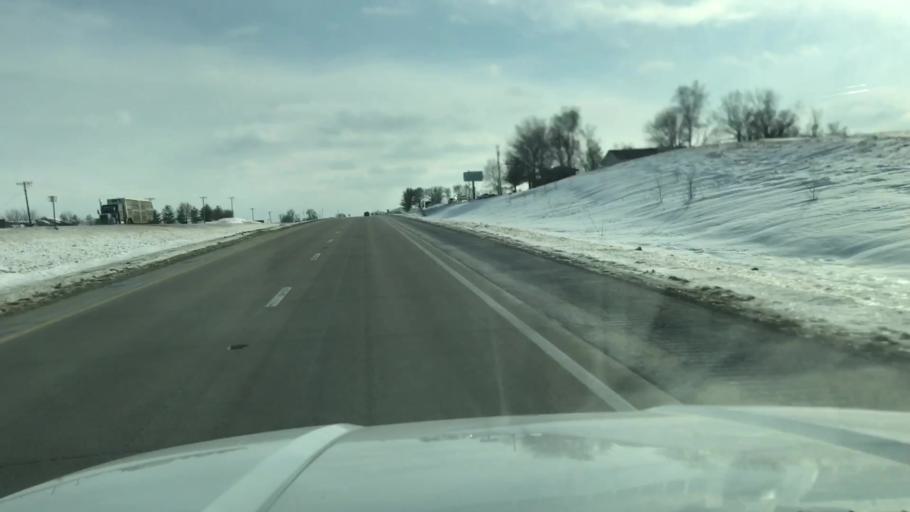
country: US
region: Missouri
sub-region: Nodaway County
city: Maryville
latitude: 40.2932
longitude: -94.8755
